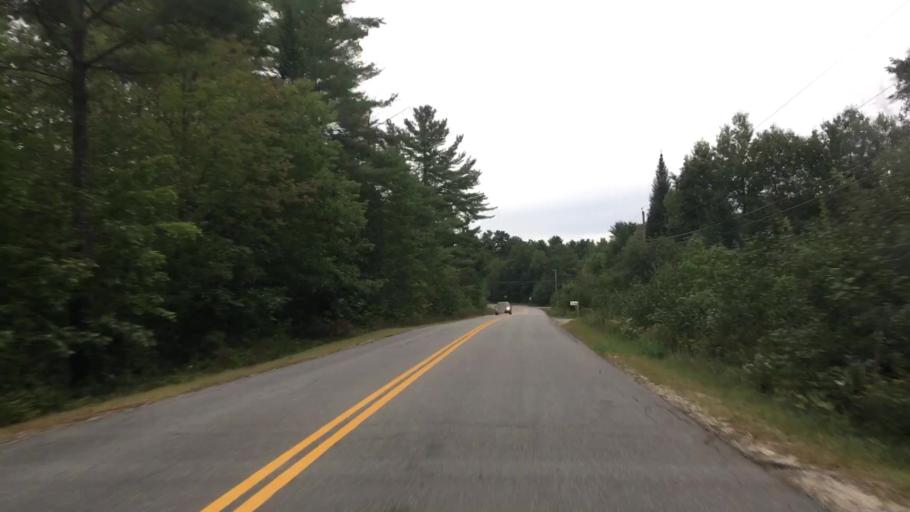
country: US
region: Maine
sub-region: Cumberland County
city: New Gloucester
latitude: 43.9030
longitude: -70.2083
